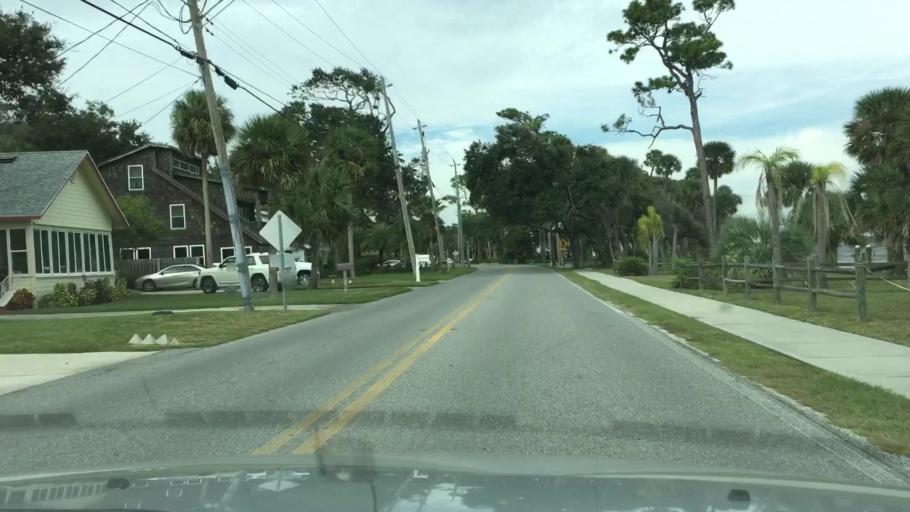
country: US
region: Florida
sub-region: Volusia County
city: Holly Hill
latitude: 29.2518
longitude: -81.0382
